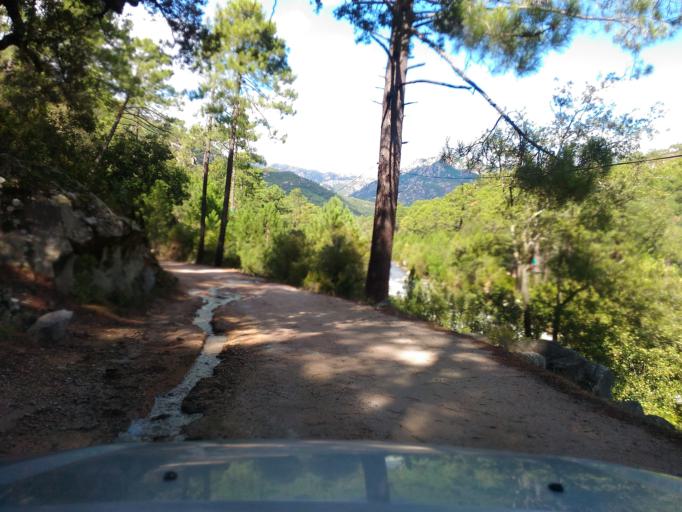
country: FR
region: Corsica
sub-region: Departement de la Corse-du-Sud
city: Porto-Vecchio
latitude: 41.7184
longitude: 9.3026
